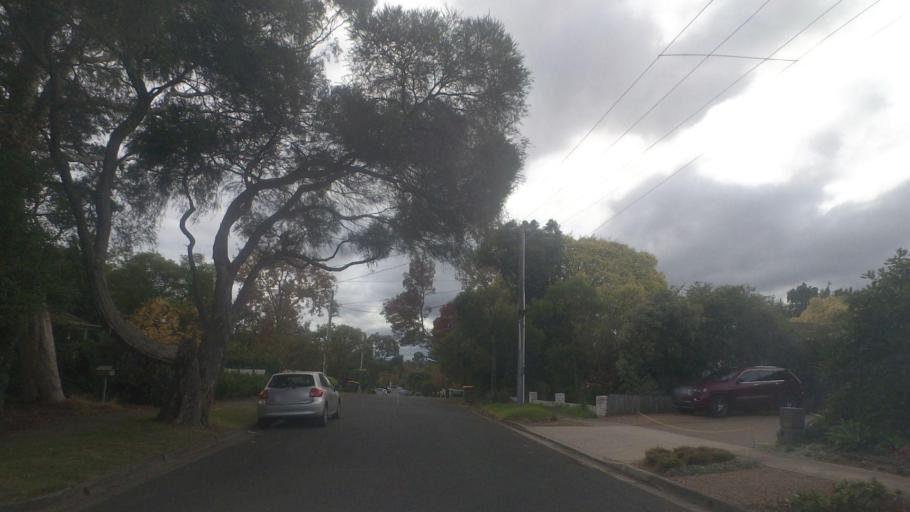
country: AU
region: Victoria
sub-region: Whitehorse
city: Blackburn South
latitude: -37.8354
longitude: 145.1483
